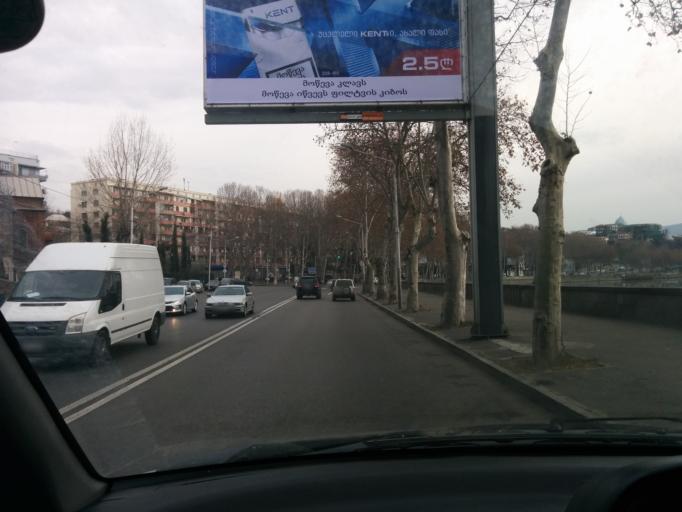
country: GE
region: T'bilisi
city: Tbilisi
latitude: 41.7016
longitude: 44.8061
